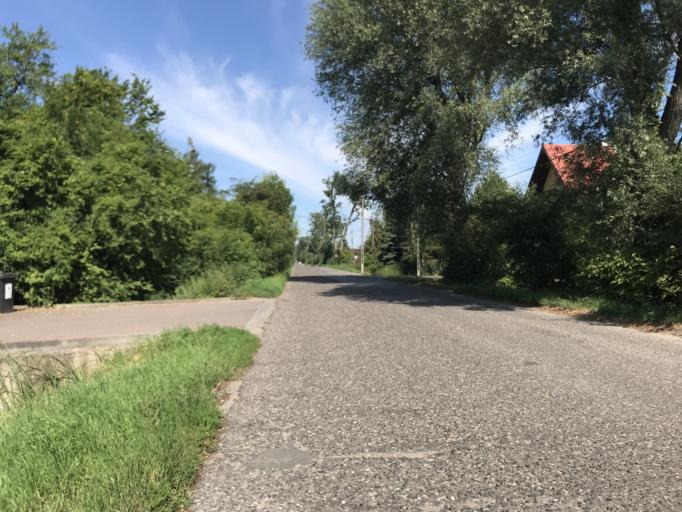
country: PL
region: Pomeranian Voivodeship
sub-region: Gdansk
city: Gdansk
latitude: 54.3217
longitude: 18.6781
